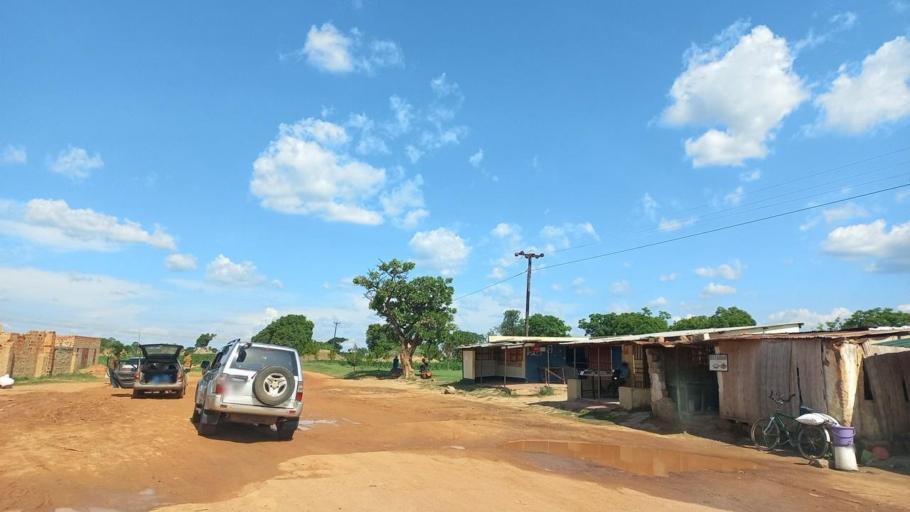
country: ZM
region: Copperbelt
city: Kitwe
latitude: -12.8716
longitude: 28.3403
